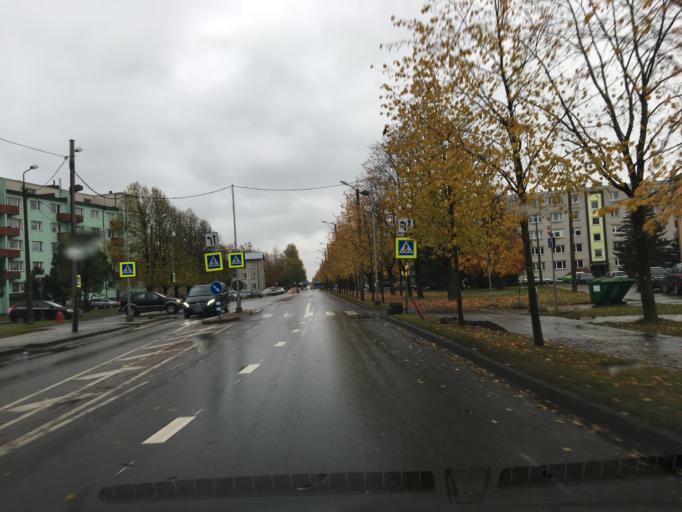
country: EE
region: Paernumaa
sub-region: Paernu linn
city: Parnu
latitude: 58.3740
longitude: 24.5311
